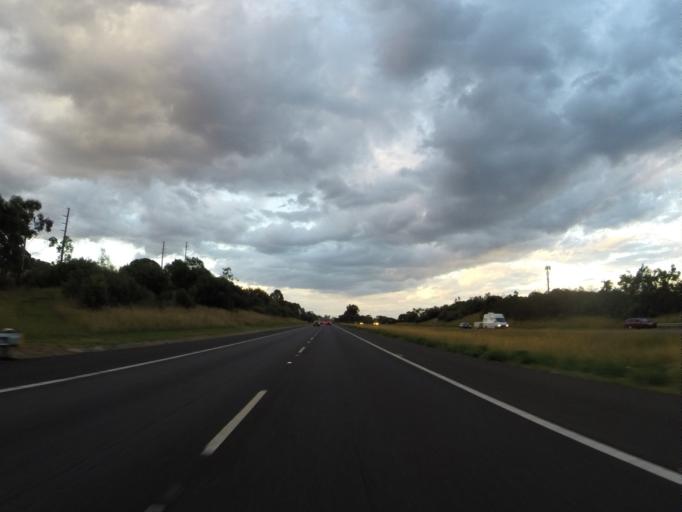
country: AU
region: New South Wales
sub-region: Campbelltown Municipality
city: Glen Alpine
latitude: -34.0761
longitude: 150.7749
